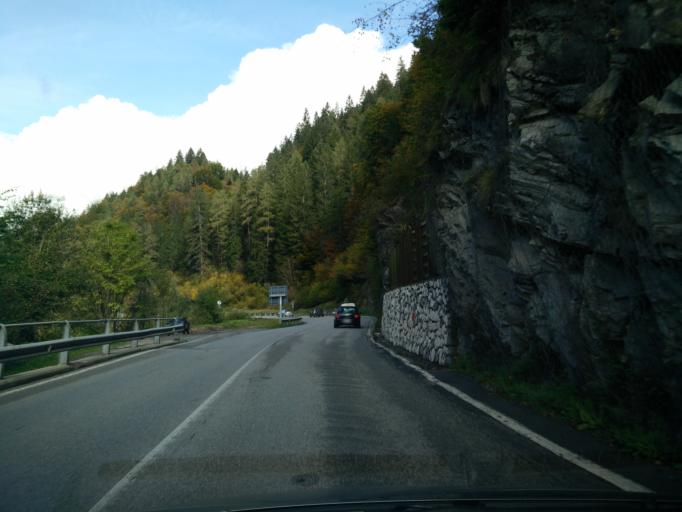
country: IT
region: Veneto
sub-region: Provincia di Belluno
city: Vigo di Cadore
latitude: 46.5362
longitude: 12.4673
